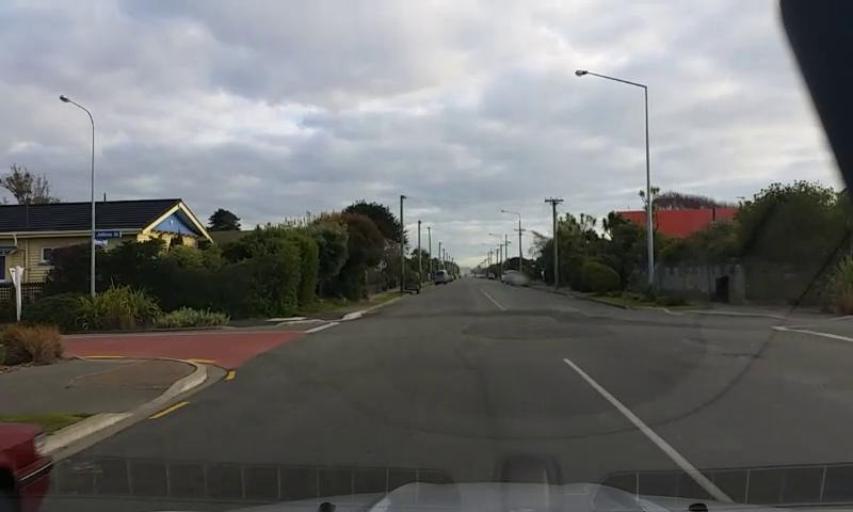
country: NZ
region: Canterbury
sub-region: Christchurch City
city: Christchurch
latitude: -43.5324
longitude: 172.7366
